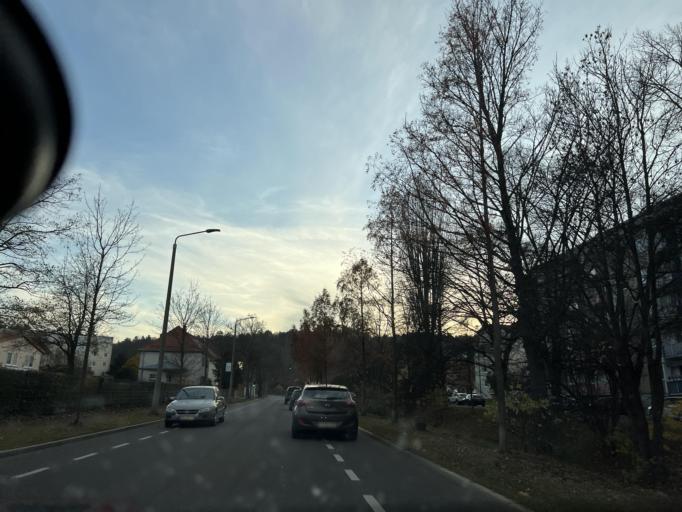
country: DE
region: Thuringia
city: Arnstadt
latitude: 50.8346
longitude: 10.9377
